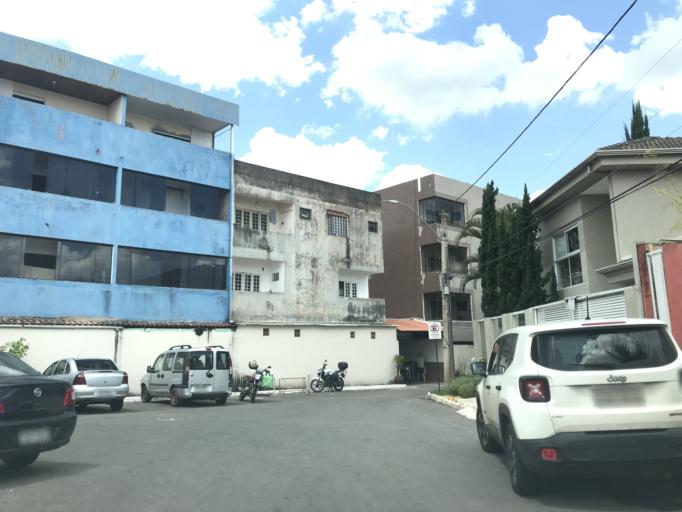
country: BR
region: Federal District
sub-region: Brasilia
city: Brasilia
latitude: -15.6821
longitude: -47.8345
